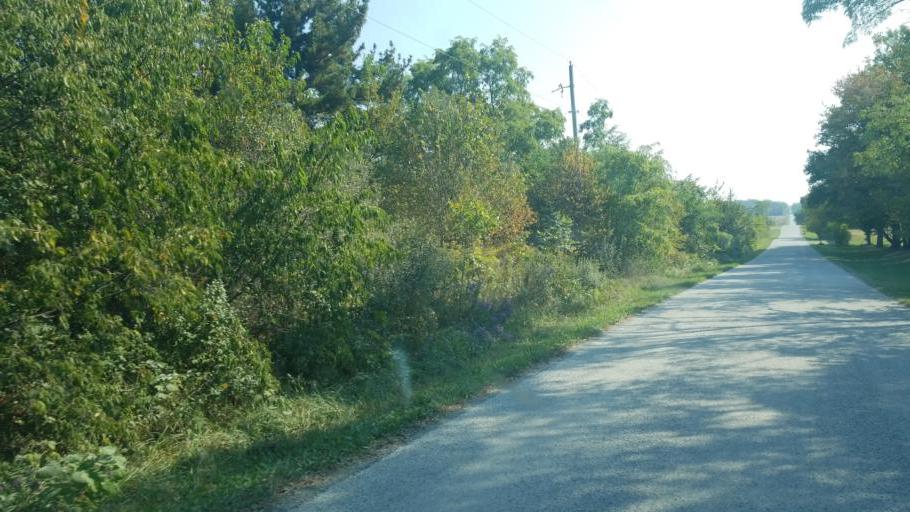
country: US
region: Ohio
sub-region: Crawford County
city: Galion
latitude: 40.6543
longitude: -82.8178
